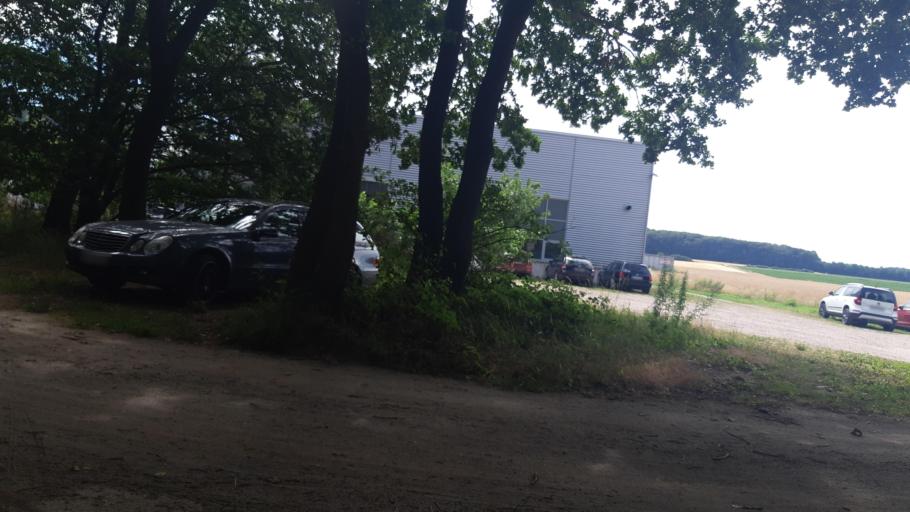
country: DE
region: Lower Saxony
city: Tosterglope
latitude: 53.2368
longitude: 10.7824
